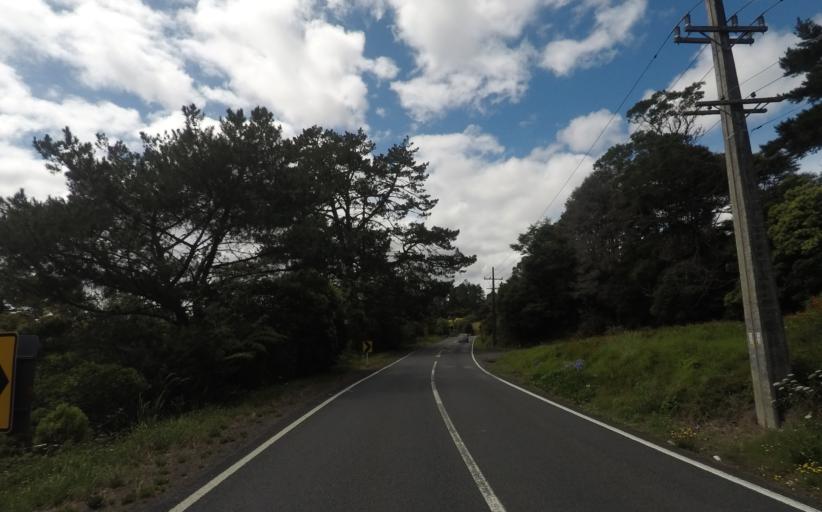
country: NZ
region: Auckland
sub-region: Auckland
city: Rosebank
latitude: -36.8631
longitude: 174.5638
